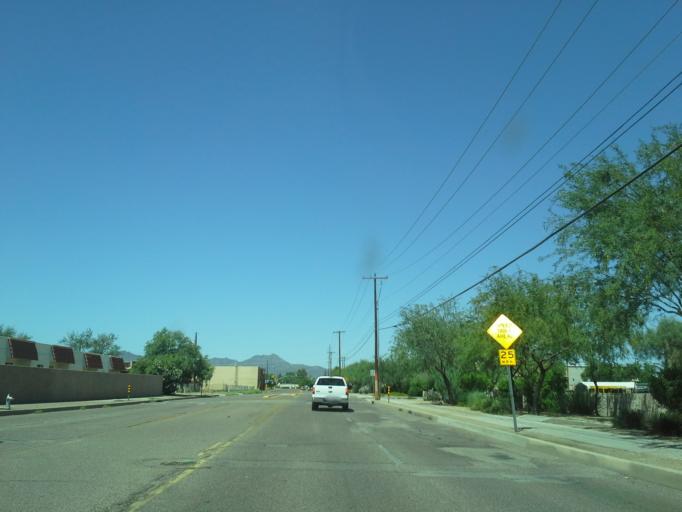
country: US
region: Arizona
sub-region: Pima County
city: Flowing Wells
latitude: 32.2829
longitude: -110.9746
